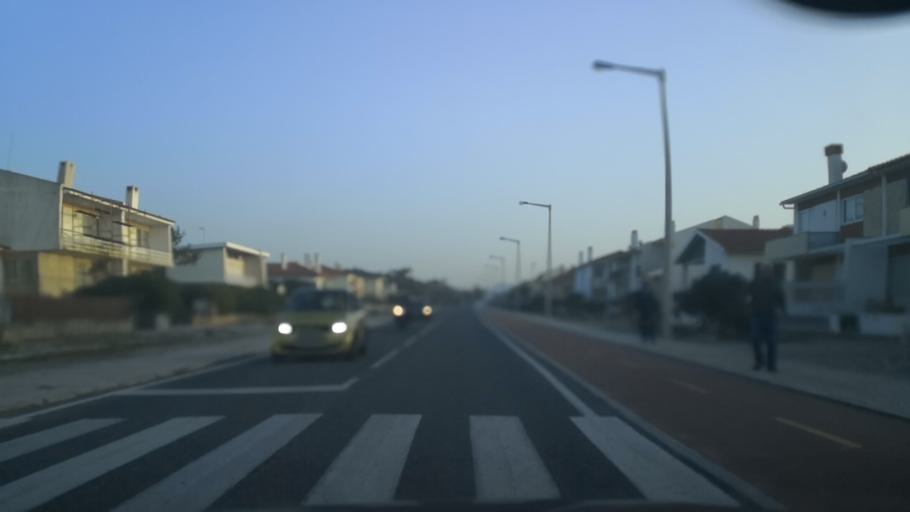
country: PT
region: Leiria
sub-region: Alcobaca
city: Pataias
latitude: 39.7611
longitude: -9.0306
